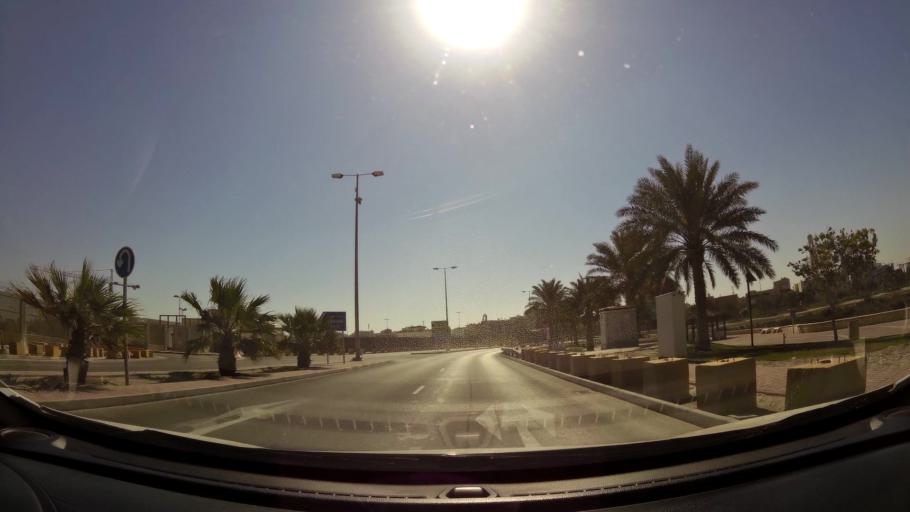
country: BH
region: Muharraq
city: Al Muharraq
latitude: 26.2626
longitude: 50.6334
